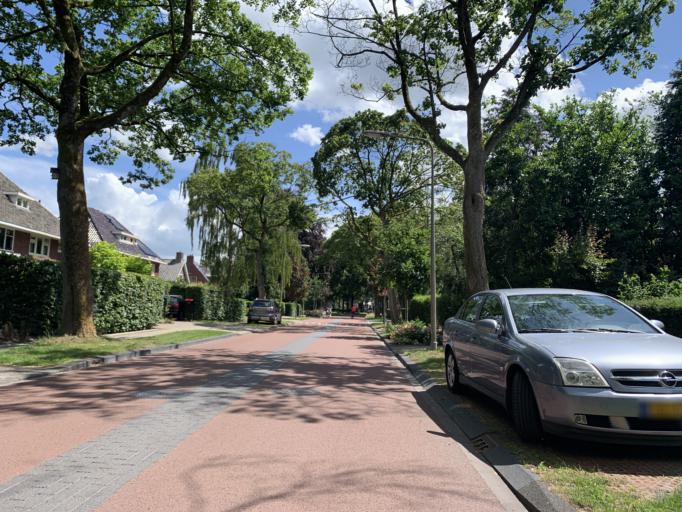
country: NL
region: Groningen
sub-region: Gemeente Haren
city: Haren
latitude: 53.1695
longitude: 6.6128
